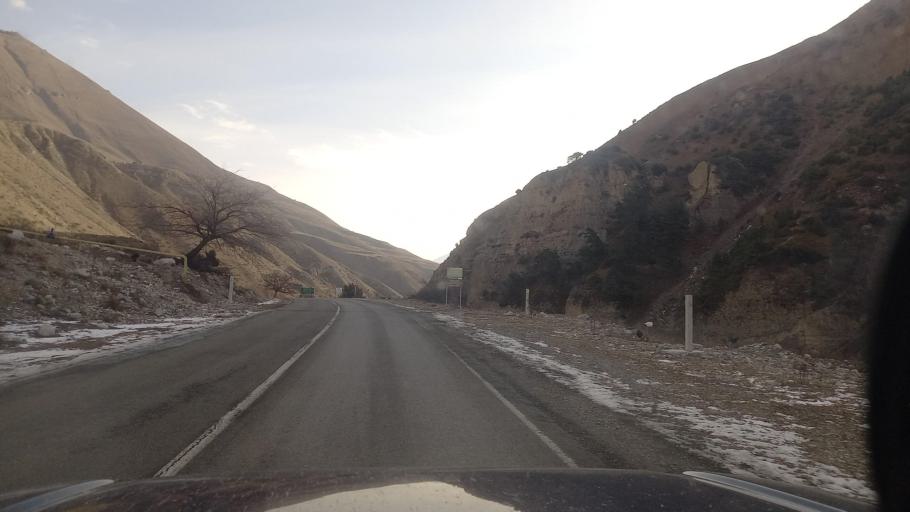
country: RU
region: Ingushetiya
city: Dzhayrakh
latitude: 42.8432
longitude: 44.6498
